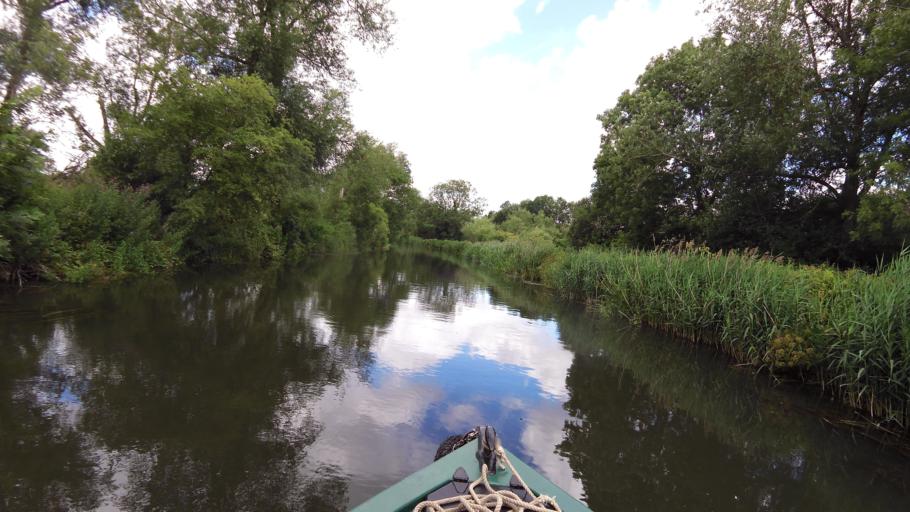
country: GB
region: England
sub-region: West Berkshire
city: Thatcham
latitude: 51.3954
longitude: -1.2807
